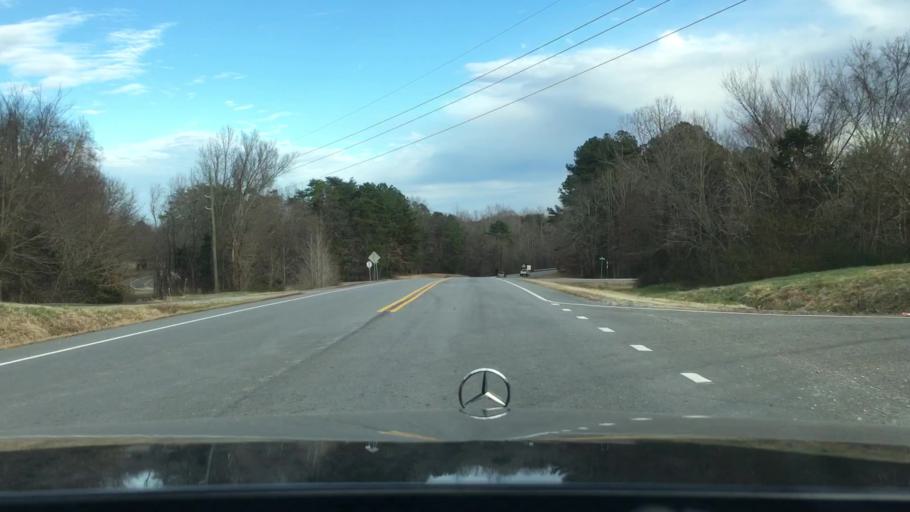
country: US
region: North Carolina
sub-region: Caswell County
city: Yanceyville
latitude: 36.4084
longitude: -79.3297
